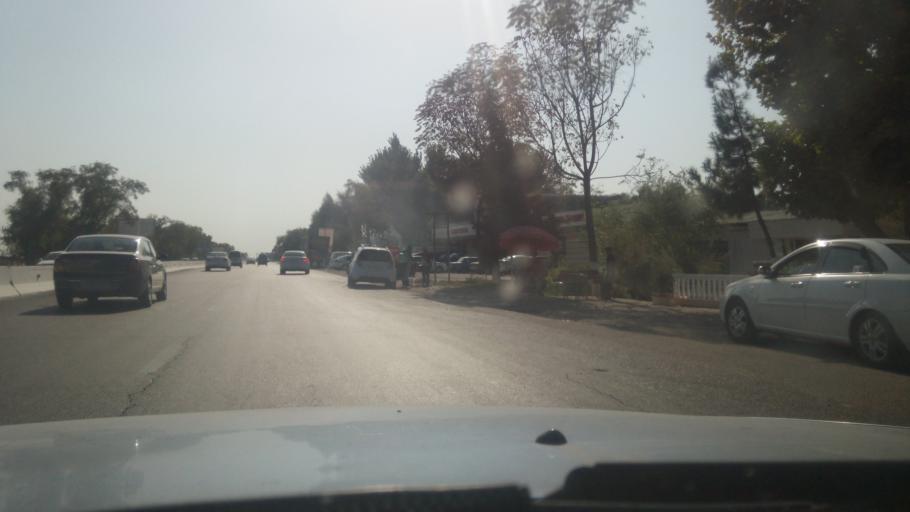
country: UZ
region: Toshkent
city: Urtaowul
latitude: 41.2266
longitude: 69.1455
